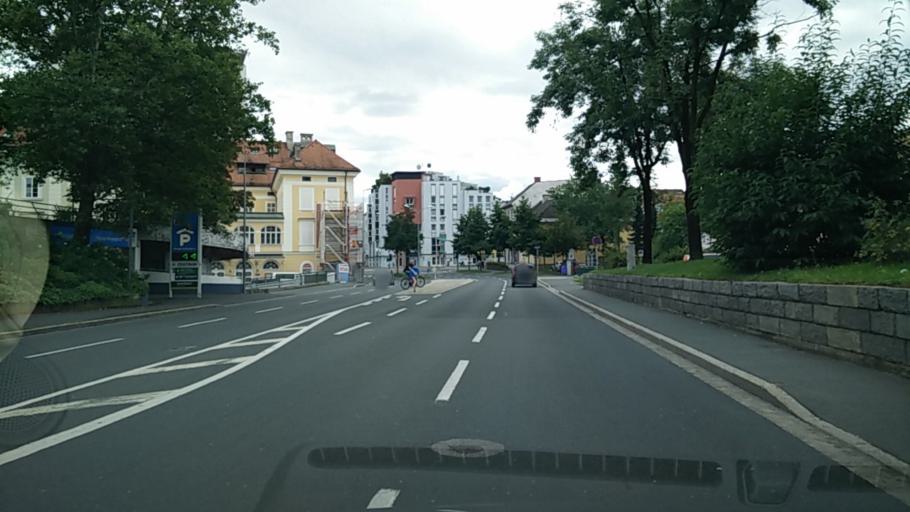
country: AT
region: Carinthia
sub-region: Klagenfurt am Woerthersee
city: Klagenfurt am Woerthersee
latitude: 46.6247
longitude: 14.3026
